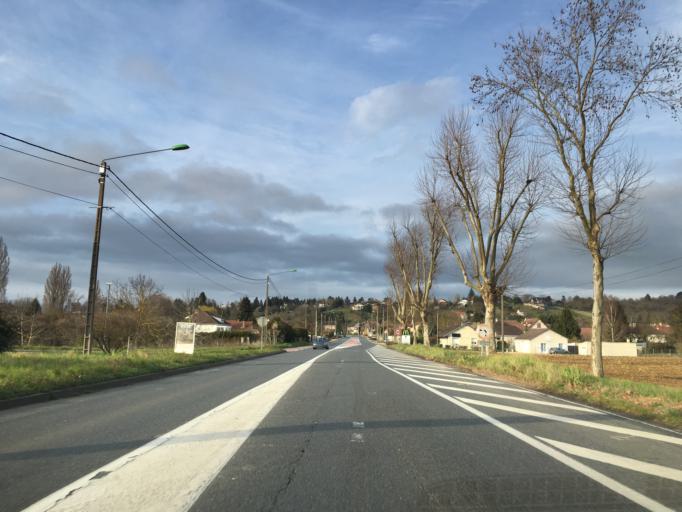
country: FR
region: Bourgogne
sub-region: Departement de l'Yonne
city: Veron
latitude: 48.1472
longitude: 3.3074
